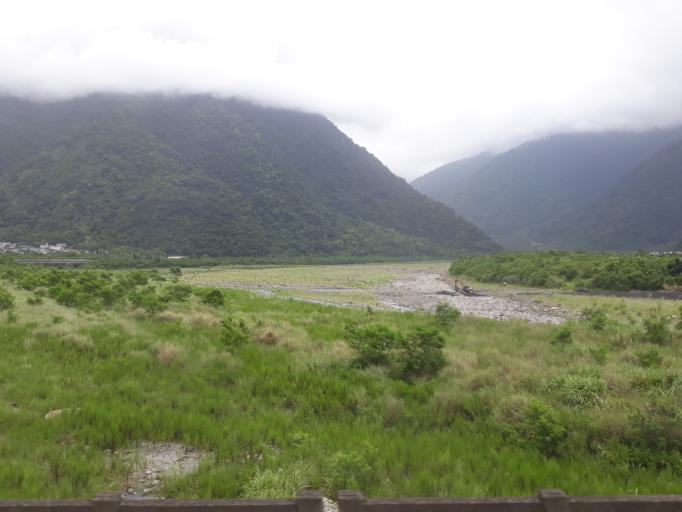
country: TW
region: Taiwan
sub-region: Yilan
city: Yilan
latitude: 24.4621
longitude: 121.7837
